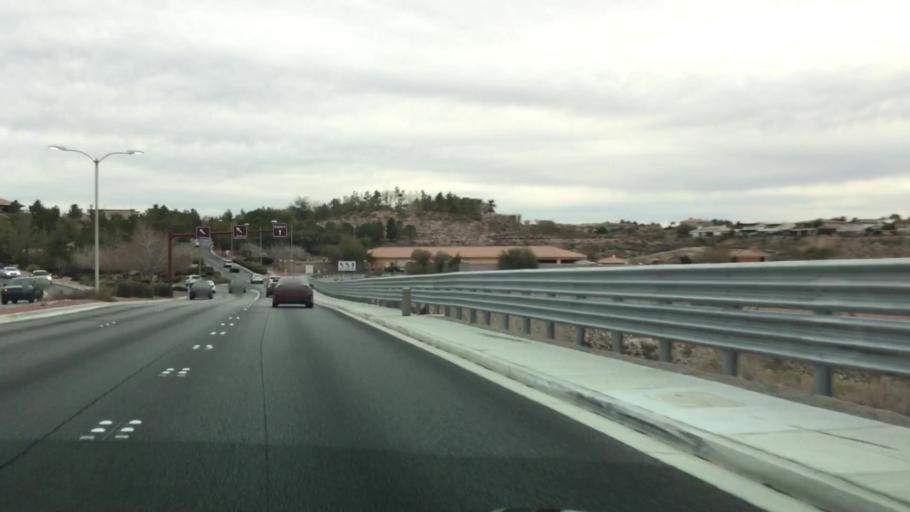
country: US
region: Nevada
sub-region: Clark County
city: Whitney
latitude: 35.9853
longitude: -115.1012
